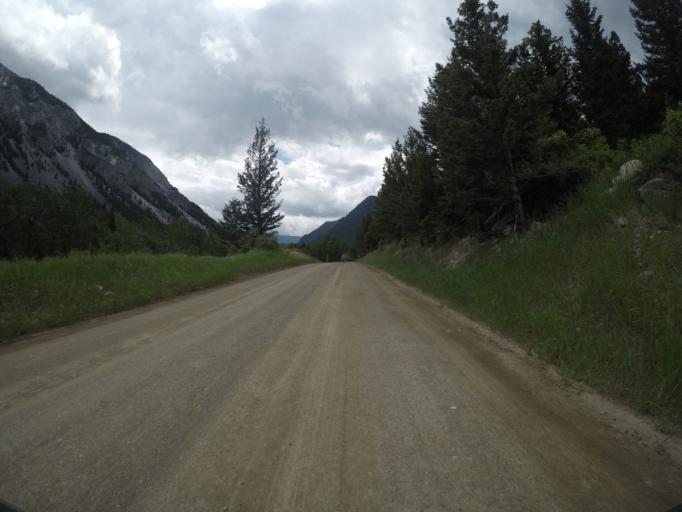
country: US
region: Montana
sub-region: Park County
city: Livingston
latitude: 45.5068
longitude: -110.2267
